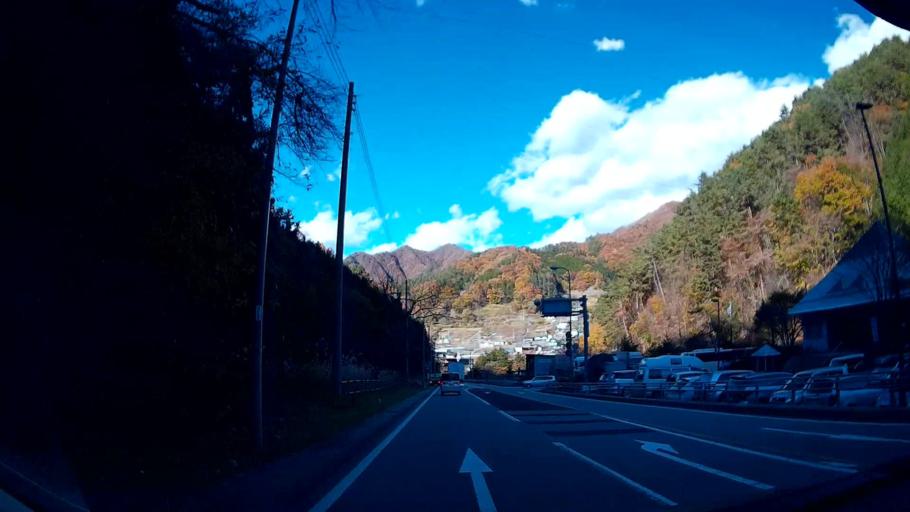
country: JP
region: Yamanashi
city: Enzan
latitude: 35.6358
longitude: 138.7926
